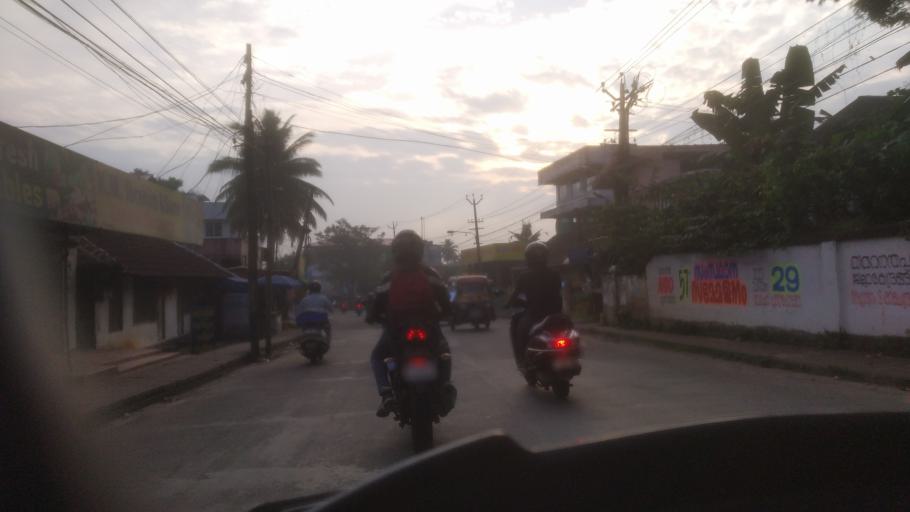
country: IN
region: Kerala
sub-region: Ernakulam
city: Aluva
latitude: 10.1069
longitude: 76.3614
